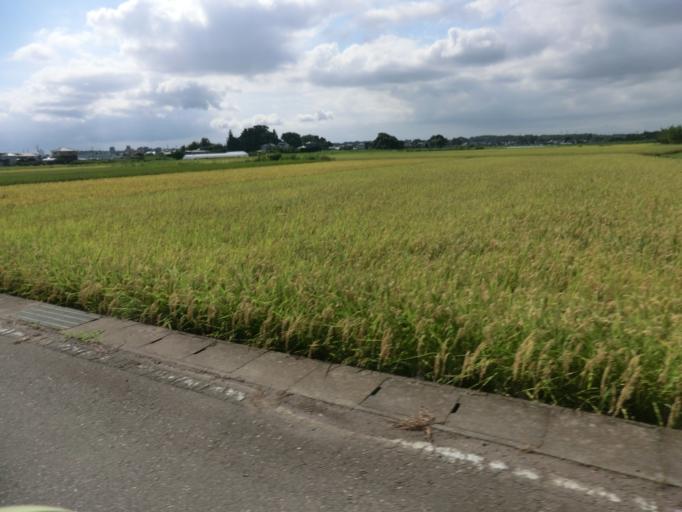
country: JP
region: Ibaraki
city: Naka
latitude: 36.0931
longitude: 140.1534
